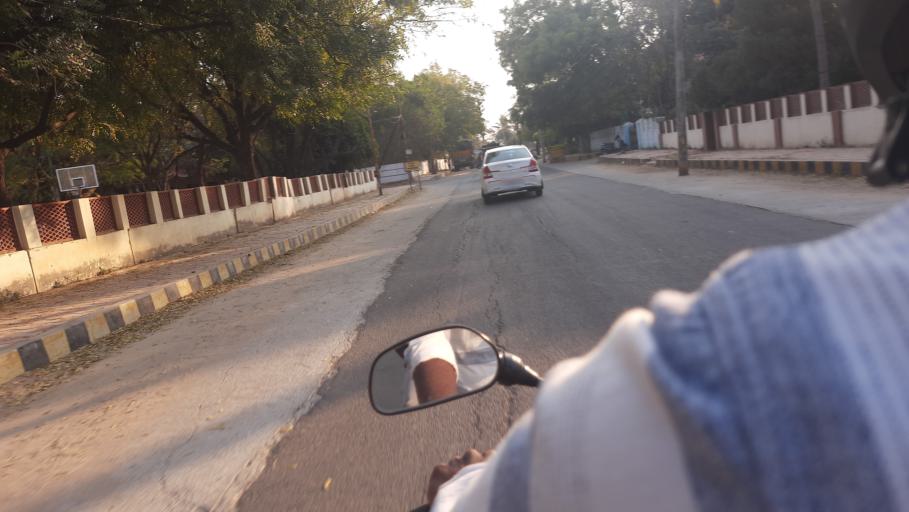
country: IN
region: Telangana
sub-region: Rangareddi
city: Secunderabad
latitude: 17.4863
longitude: 78.5477
